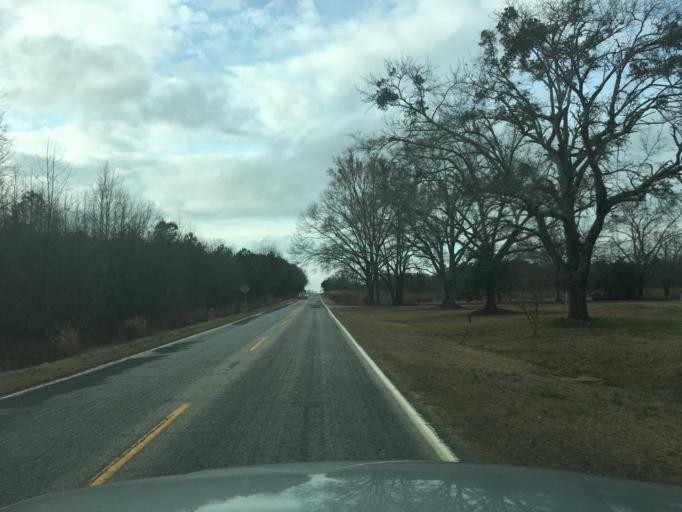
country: US
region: South Carolina
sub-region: Abbeville County
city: Due West
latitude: 34.3240
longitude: -82.4713
